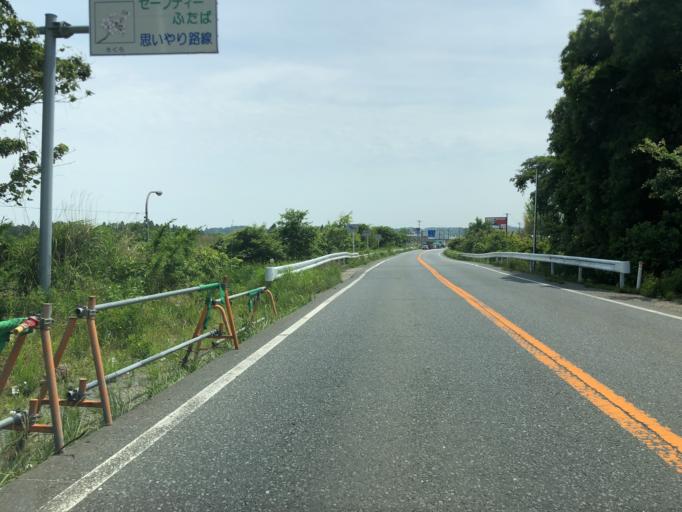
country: JP
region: Fukushima
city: Namie
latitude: 37.4607
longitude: 141.0103
